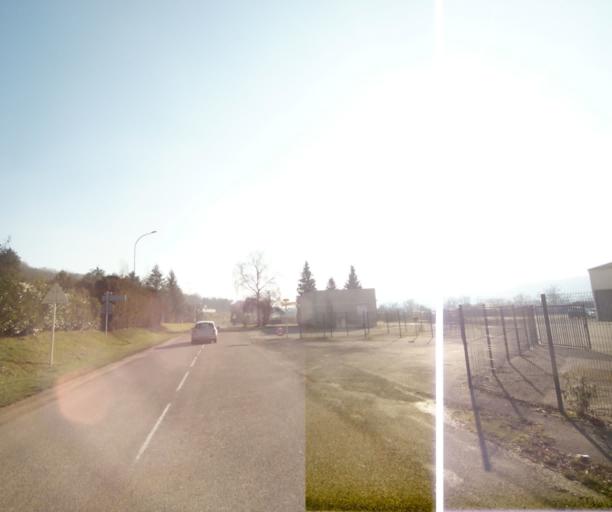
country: FR
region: Champagne-Ardenne
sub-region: Departement de la Haute-Marne
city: Chevillon
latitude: 48.5199
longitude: 5.1178
